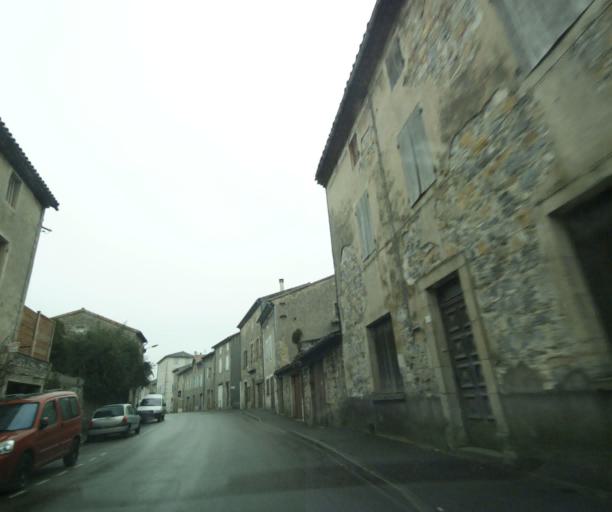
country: FR
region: Rhone-Alpes
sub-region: Departement de l'Ardeche
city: Saint-Privat
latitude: 44.6265
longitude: 4.4087
